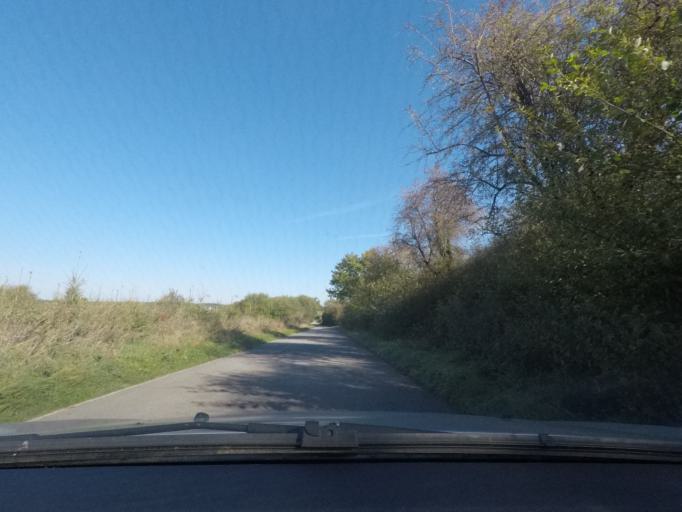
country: BE
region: Wallonia
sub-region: Province du Luxembourg
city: Etalle
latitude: 49.7126
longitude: 5.5660
